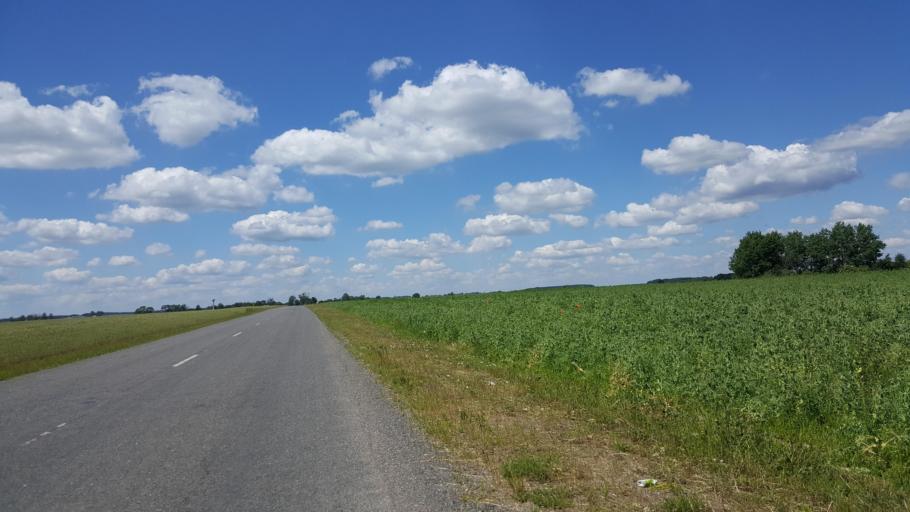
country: PL
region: Podlasie
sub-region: Powiat hajnowski
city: Czeremcha
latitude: 52.4762
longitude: 23.4992
